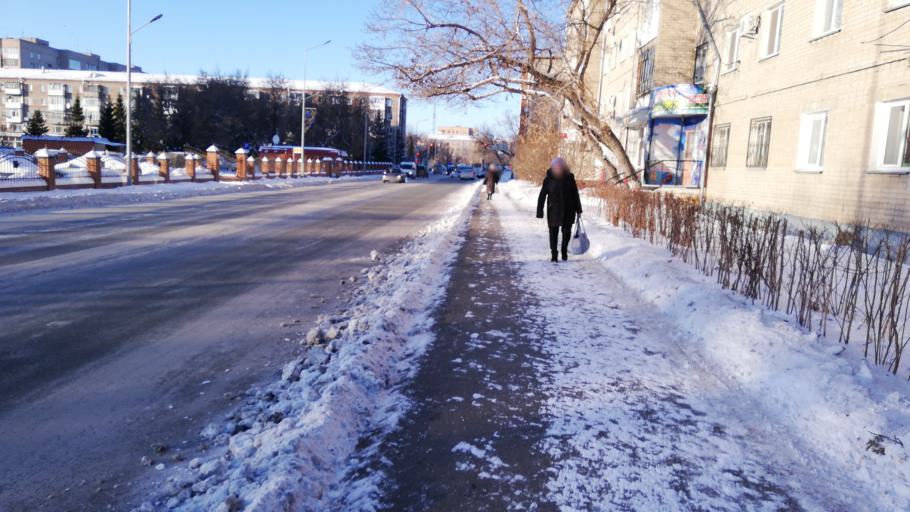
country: KZ
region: Soltustik Qazaqstan
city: Petropavlovsk
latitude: 54.8639
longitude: 69.1419
